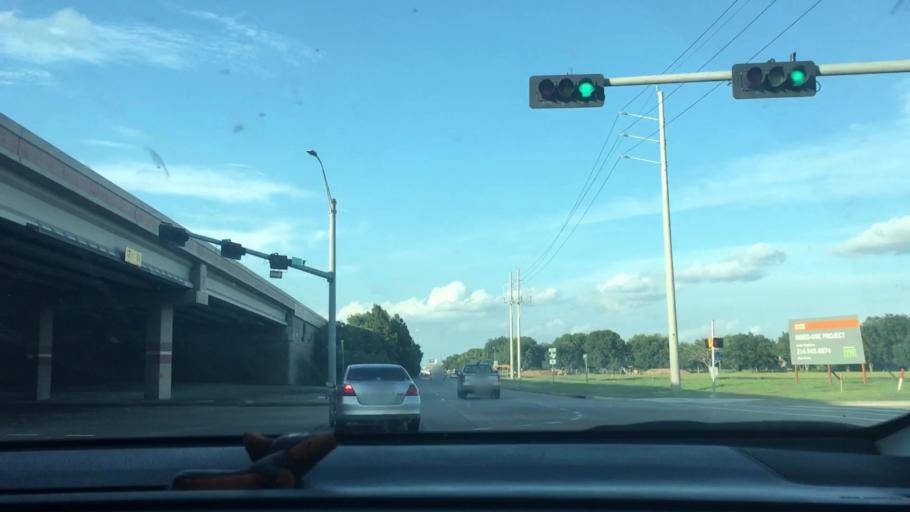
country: US
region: Texas
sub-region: Fort Bend County
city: Meadows Place
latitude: 29.6386
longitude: -95.5814
